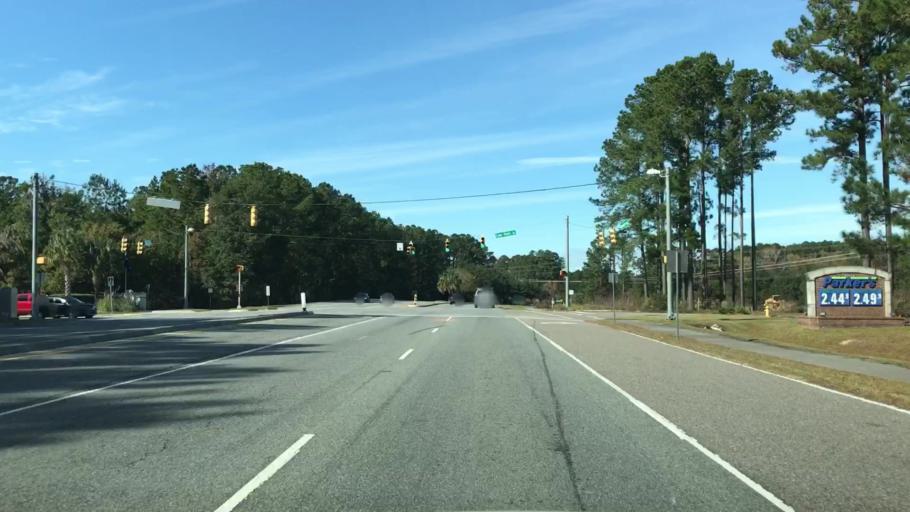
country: US
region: South Carolina
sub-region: Beaufort County
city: Bluffton
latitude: 32.2651
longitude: -80.9108
